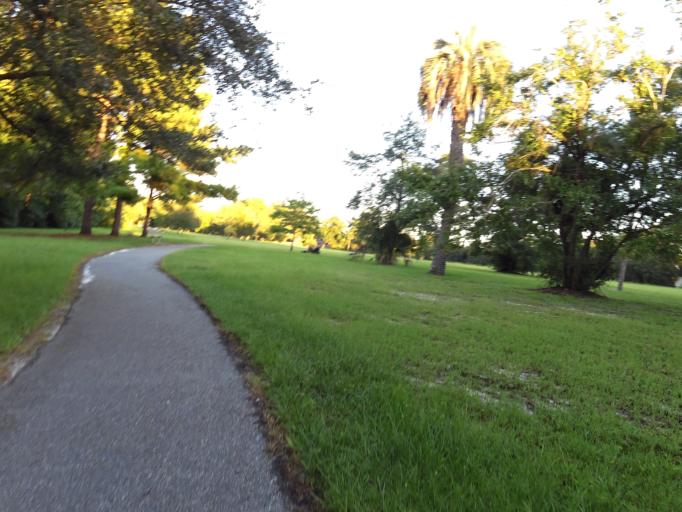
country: US
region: Florida
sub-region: Duval County
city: Jacksonville
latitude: 30.3016
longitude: -81.6479
